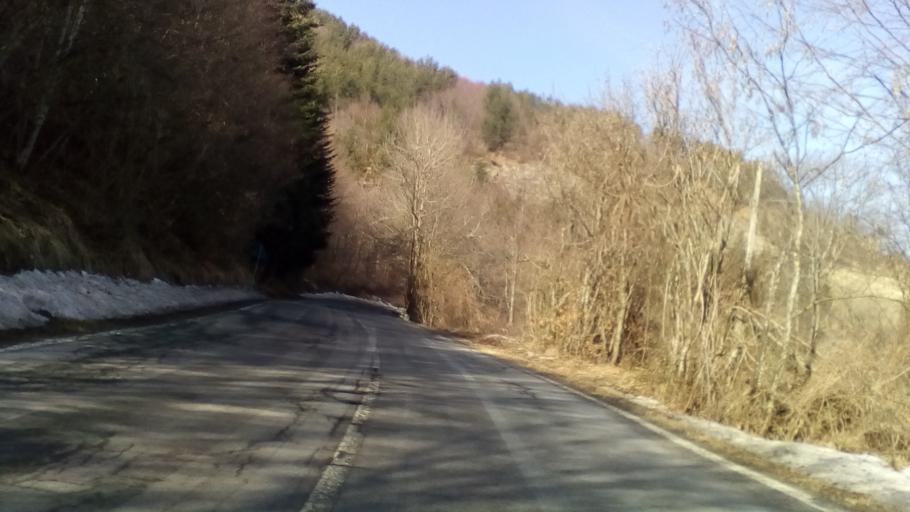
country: IT
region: Emilia-Romagna
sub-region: Provincia di Modena
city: Pievepelago
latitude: 44.2241
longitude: 10.6282
